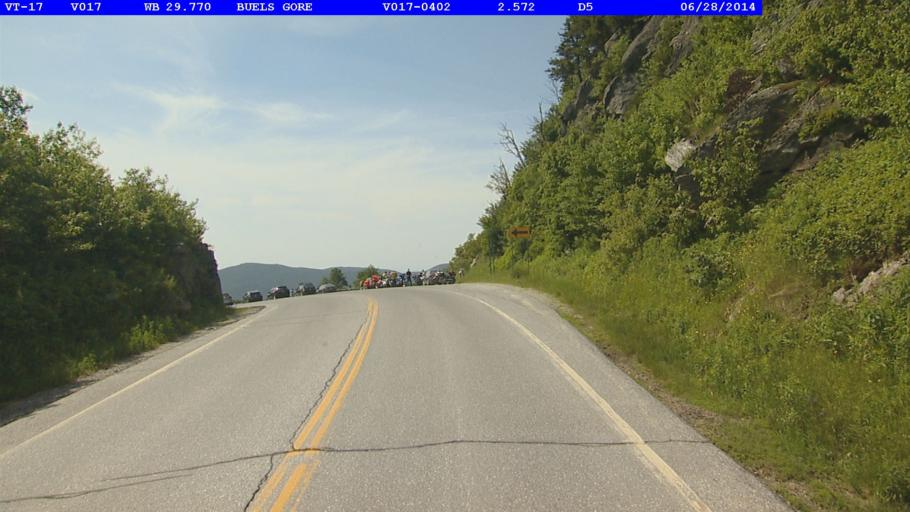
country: US
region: Vermont
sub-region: Addison County
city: Bristol
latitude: 44.2109
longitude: -72.9307
